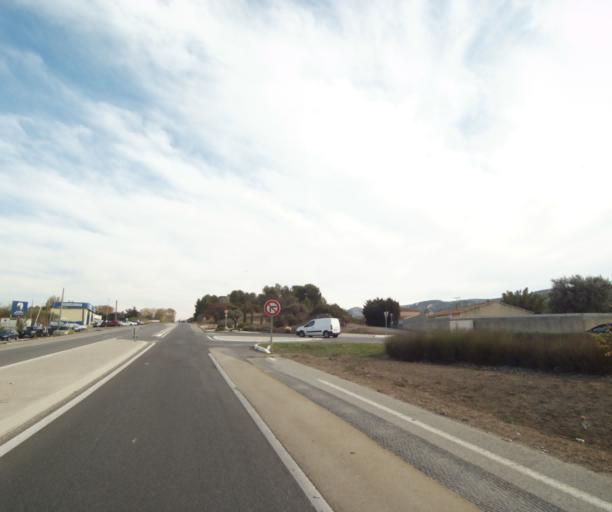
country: FR
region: Provence-Alpes-Cote d'Azur
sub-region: Departement des Bouches-du-Rhone
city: Gignac-la-Nerthe
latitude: 43.3965
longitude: 5.2453
